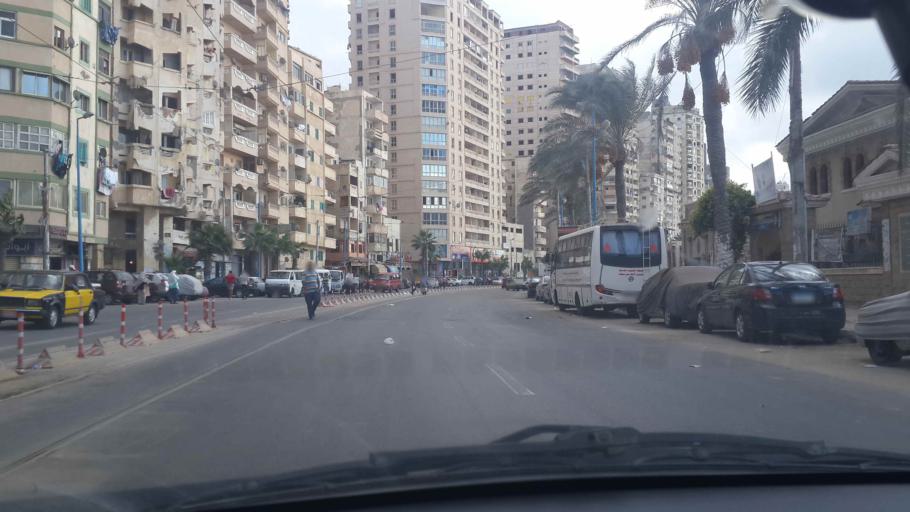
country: EG
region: Alexandria
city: Alexandria
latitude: 31.2063
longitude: 29.8787
